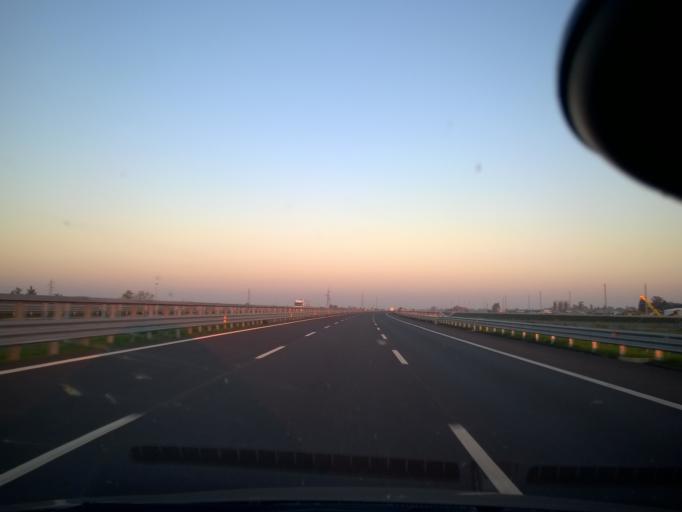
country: IT
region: Lombardy
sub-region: Provincia di Bergamo
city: Antegnate
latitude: 45.4957
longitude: 9.8113
